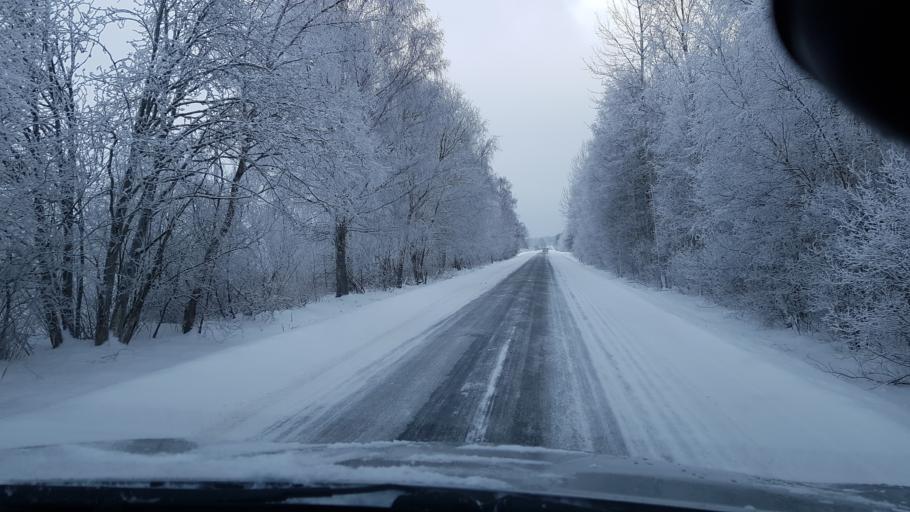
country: EE
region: Harju
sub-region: Keila linn
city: Keila
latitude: 59.3303
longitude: 24.4011
